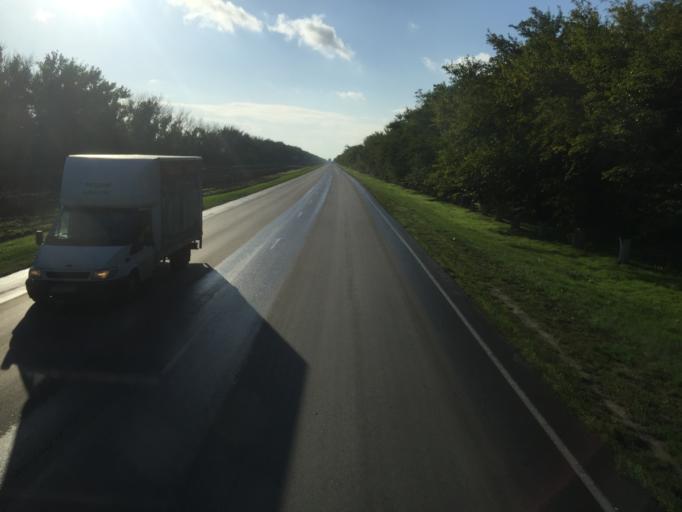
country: RU
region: Rostov
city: Yegorlykskaya
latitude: 46.6169
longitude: 40.6011
